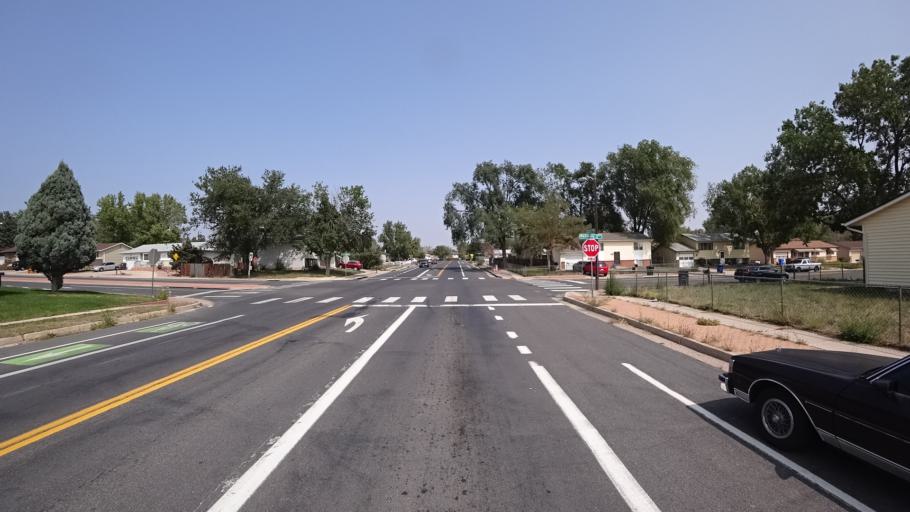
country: US
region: Colorado
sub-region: El Paso County
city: Stratmoor
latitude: 38.7961
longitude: -104.7660
